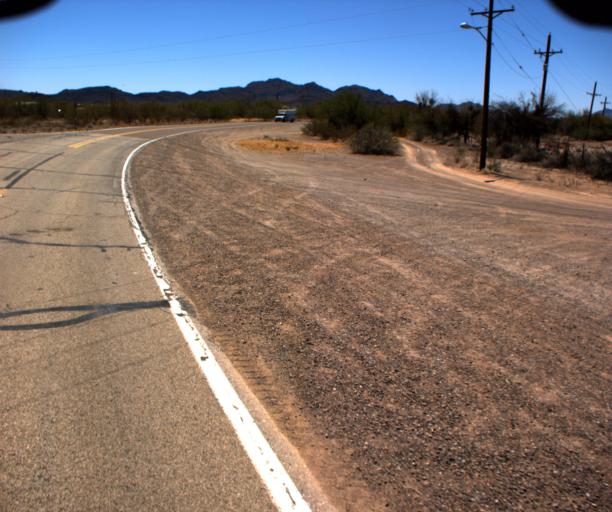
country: US
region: Arizona
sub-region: Pima County
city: Ajo
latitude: 32.2650
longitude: -112.7380
